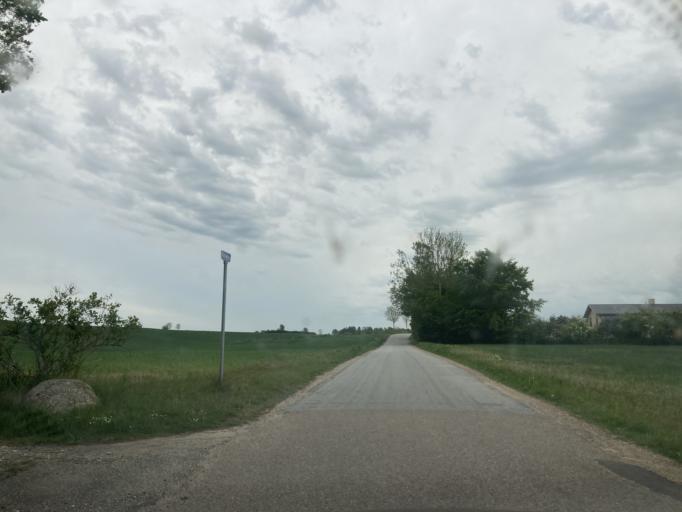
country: DK
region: Zealand
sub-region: Roskilde Kommune
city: Svogerslev
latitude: 55.6778
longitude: 11.9990
